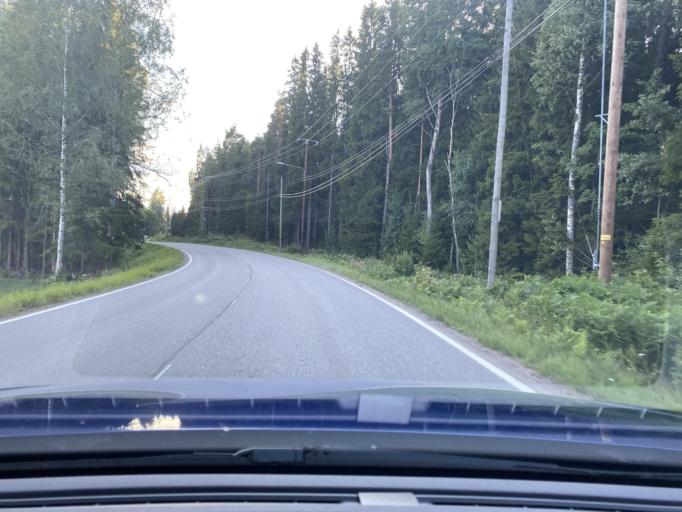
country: FI
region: Uusimaa
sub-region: Helsinki
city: Nurmijaervi
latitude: 60.4057
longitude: 24.7946
